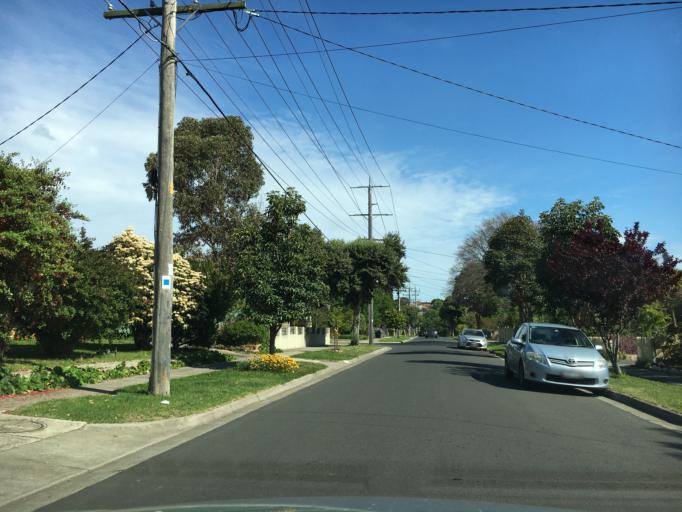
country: AU
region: Victoria
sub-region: Monash
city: Chadstone
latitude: -37.8959
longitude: 145.1142
